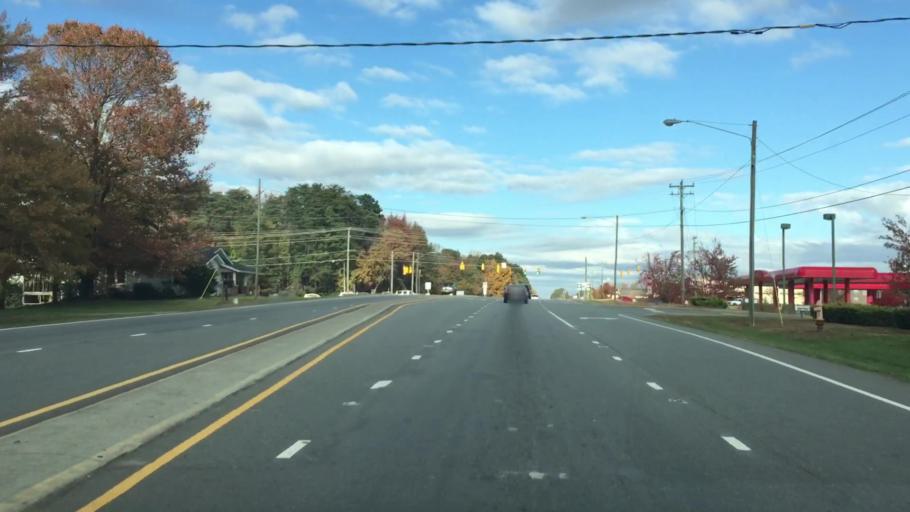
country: US
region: North Carolina
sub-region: Forsyth County
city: Walkertown
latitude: 36.1639
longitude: -80.1384
